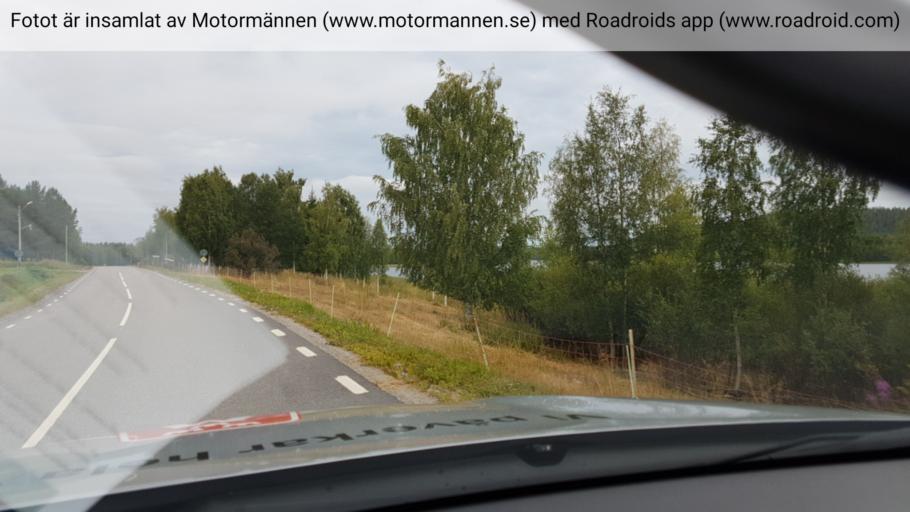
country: SE
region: Norrbotten
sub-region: Bodens Kommun
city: Boden
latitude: 65.7282
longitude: 21.6024
